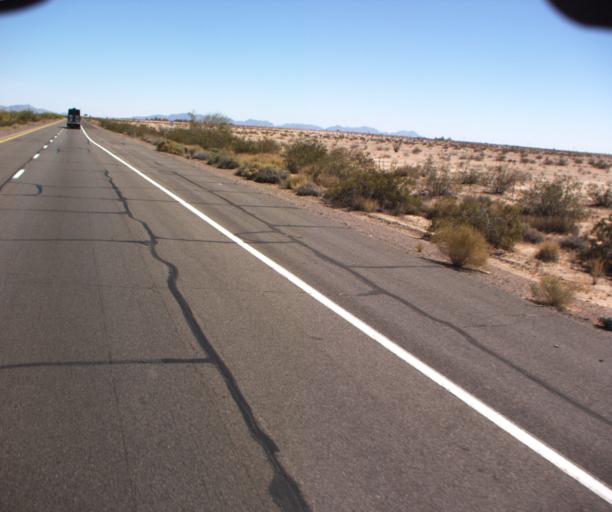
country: US
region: Arizona
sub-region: Yuma County
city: Wellton
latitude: 32.6826
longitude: -114.0164
